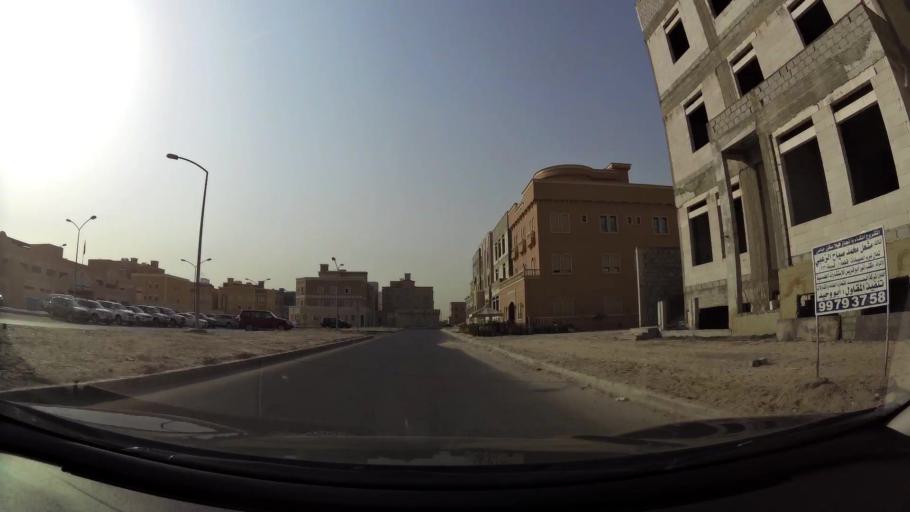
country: KW
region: Al Asimah
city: Ar Rabiyah
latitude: 29.3243
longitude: 47.8084
